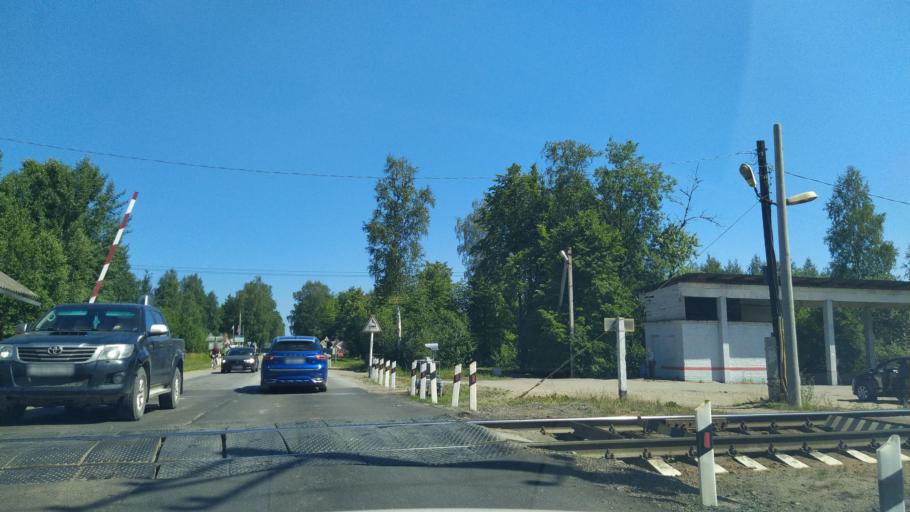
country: RU
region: Leningrad
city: Imeni Morozova
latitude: 59.9697
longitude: 31.0217
